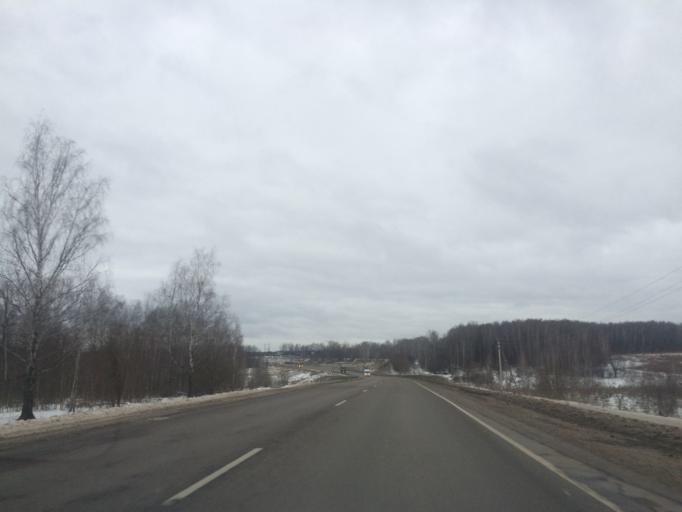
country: RU
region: Tula
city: Kosaya Gora
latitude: 54.1512
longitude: 37.4249
